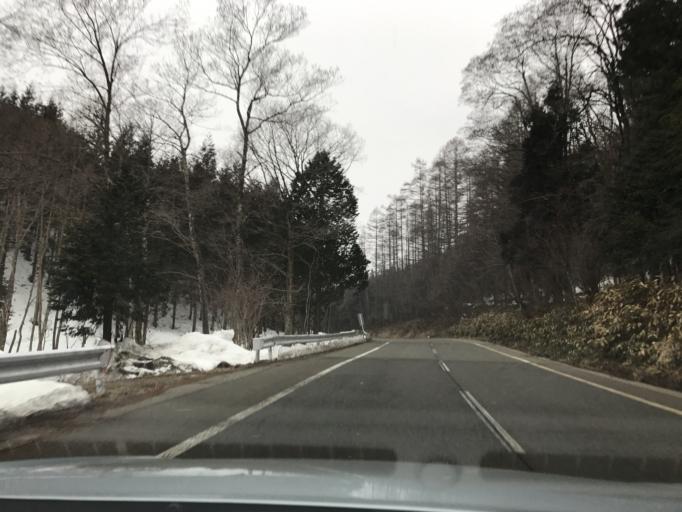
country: JP
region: Nagano
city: Omachi
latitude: 36.5788
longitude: 137.8806
